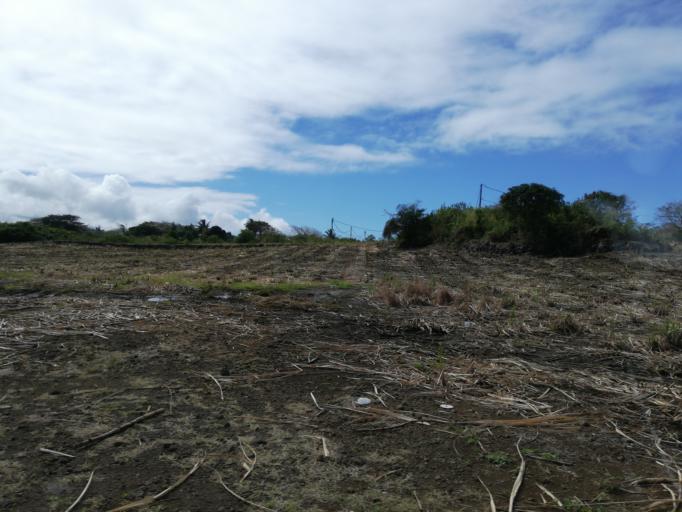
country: MU
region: Grand Port
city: Plaine Magnien
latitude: -20.4672
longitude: 57.6749
